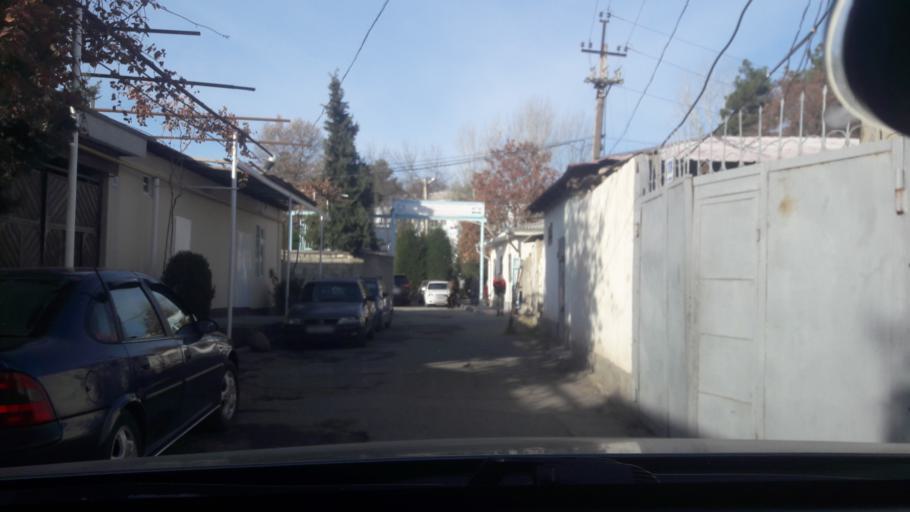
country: TJ
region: Dushanbe
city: Dushanbe
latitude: 38.5813
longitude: 68.7600
